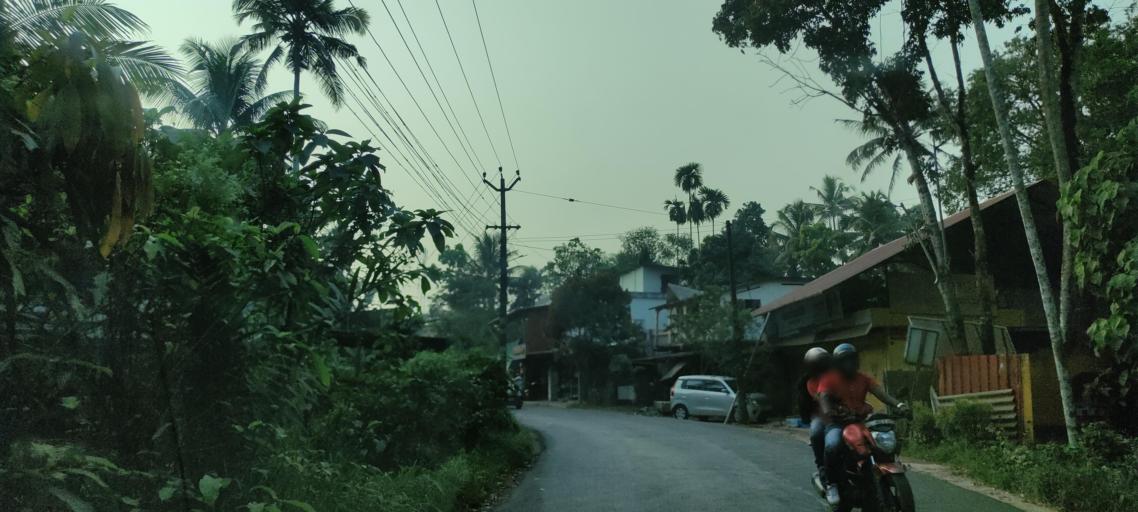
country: IN
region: Kerala
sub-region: Kottayam
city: Vaikam
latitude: 9.6867
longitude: 76.4216
